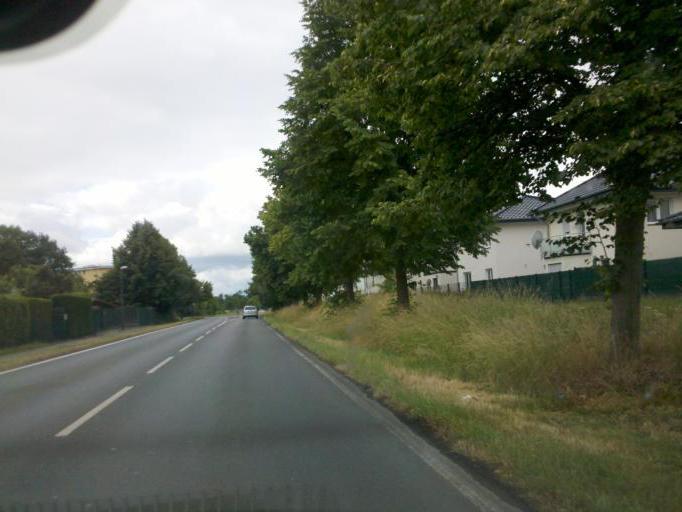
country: DE
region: North Rhine-Westphalia
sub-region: Regierungsbezirk Arnsberg
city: Lippstadt
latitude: 51.6559
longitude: 8.3356
